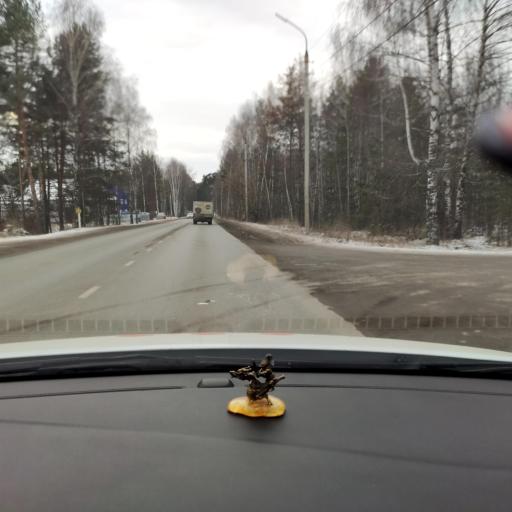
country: RU
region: Tatarstan
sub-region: Zelenodol'skiy Rayon
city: Zelenodolsk
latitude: 55.8661
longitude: 48.5385
